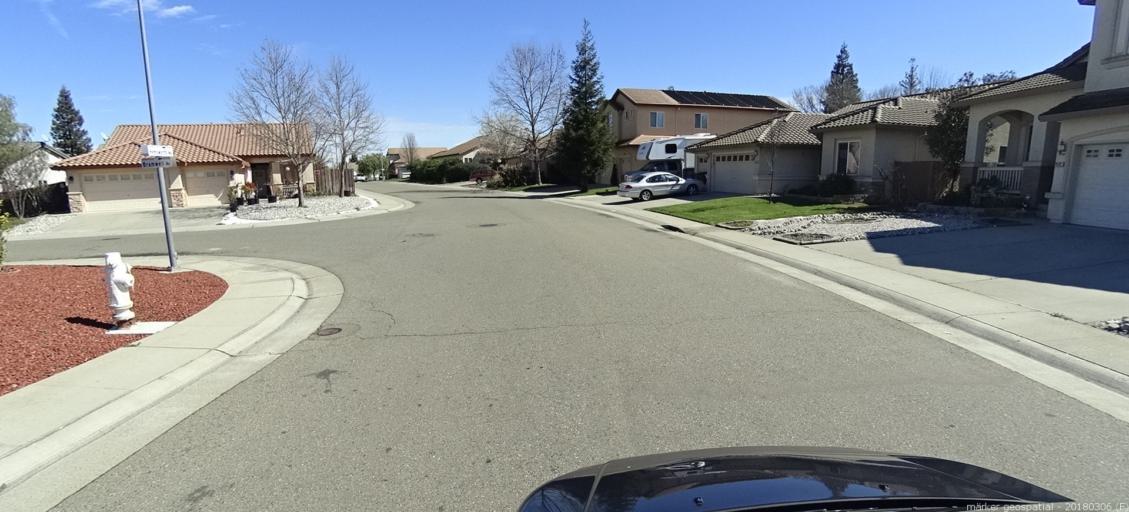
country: US
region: California
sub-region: Sacramento County
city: Vineyard
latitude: 38.4679
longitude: -121.3606
